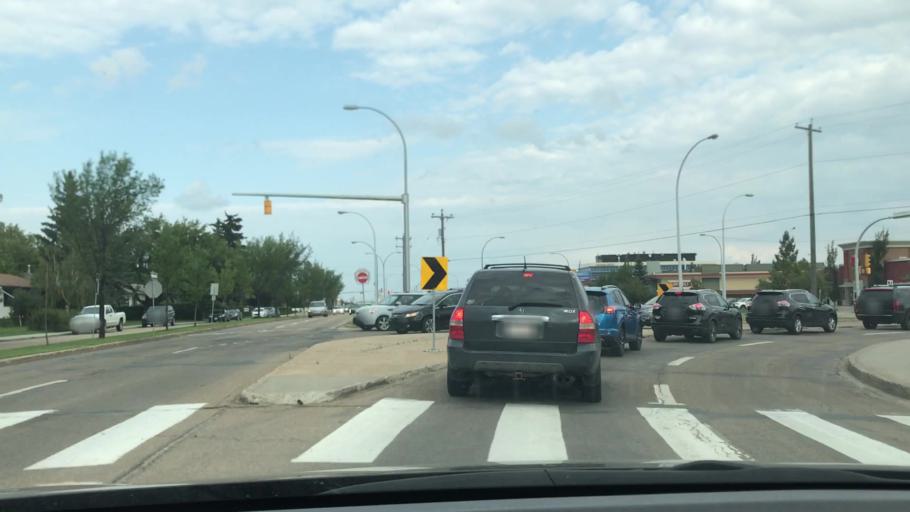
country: CA
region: Alberta
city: Edmonton
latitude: 53.5412
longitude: -113.4238
